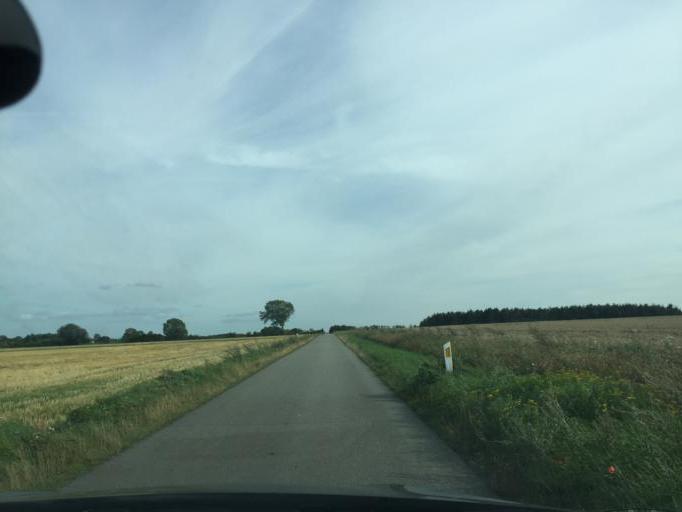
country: DK
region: South Denmark
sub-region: Kerteminde Kommune
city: Langeskov
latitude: 55.3377
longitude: 10.5510
